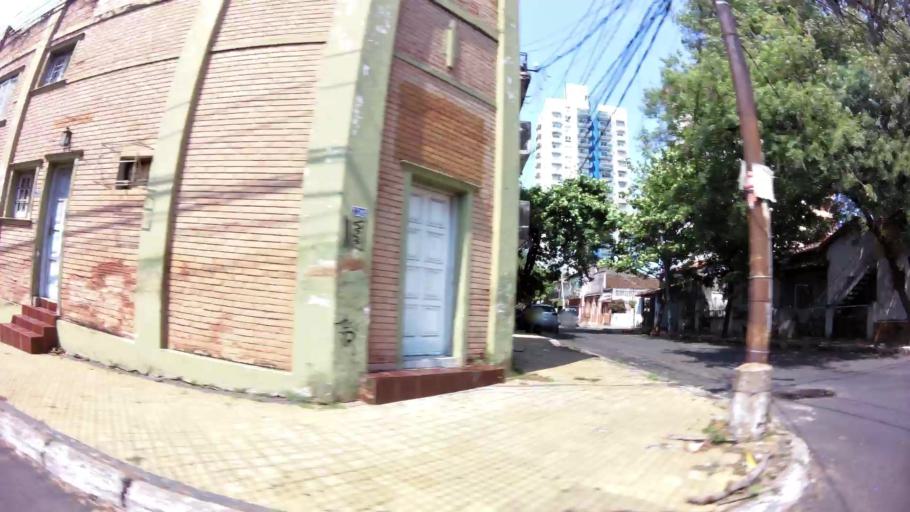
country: PY
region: Asuncion
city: Asuncion
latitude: -25.2892
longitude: -57.6459
